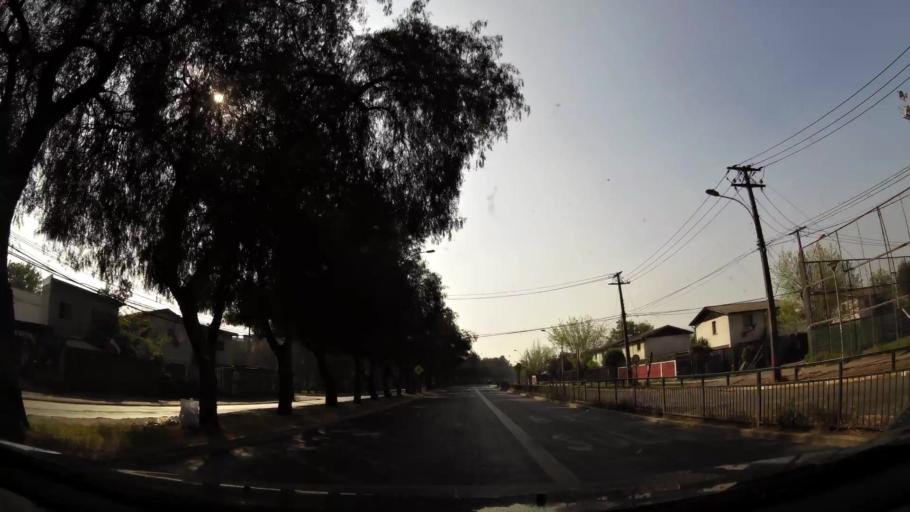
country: CL
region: Santiago Metropolitan
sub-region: Provincia de Santiago
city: Lo Prado
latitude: -33.3720
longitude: -70.6873
